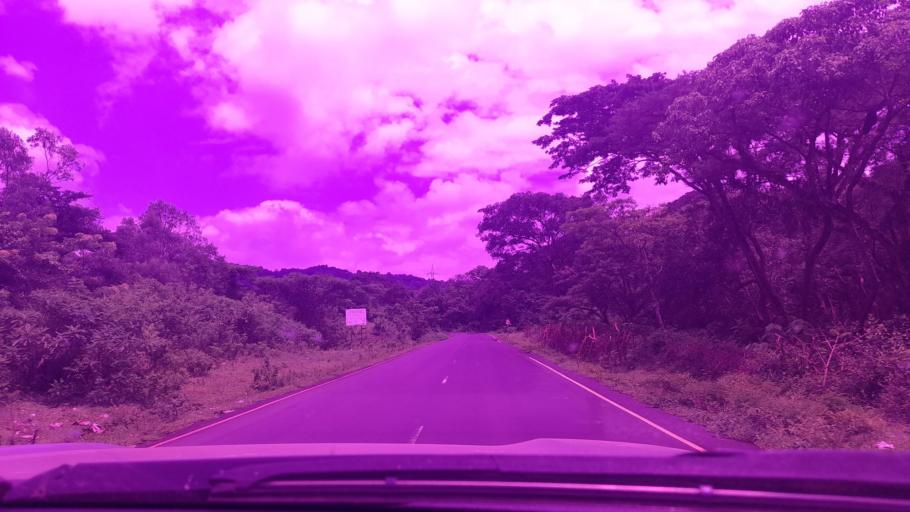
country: ET
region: Oromiya
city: Metu
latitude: 8.3288
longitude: 35.7624
